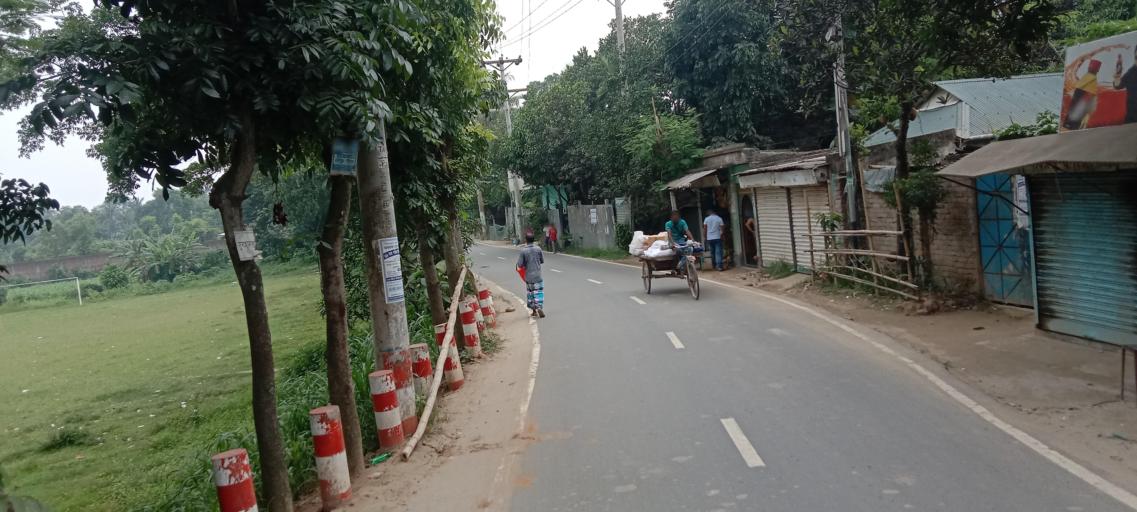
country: BD
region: Dhaka
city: Azimpur
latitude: 23.7287
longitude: 90.2732
